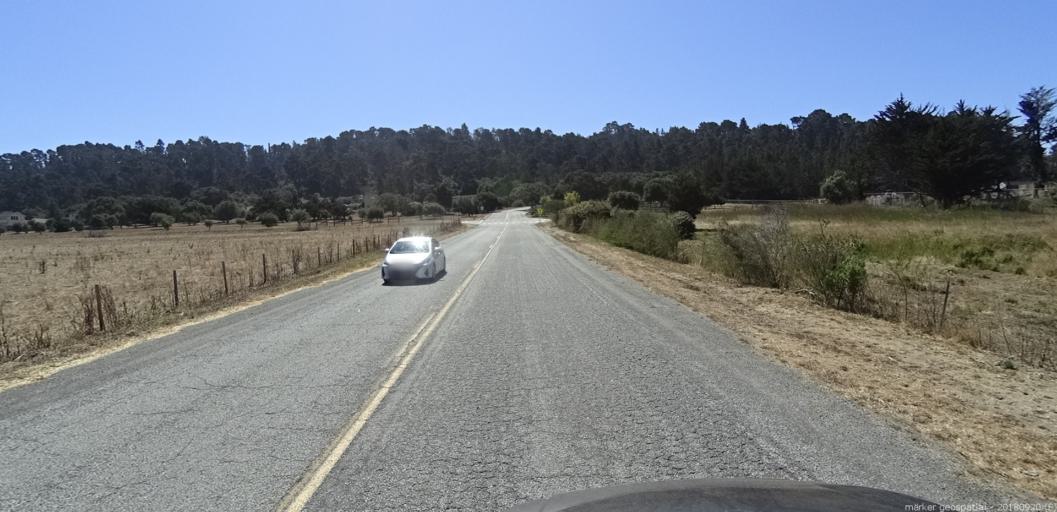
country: US
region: California
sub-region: Monterey County
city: Del Rey Oaks
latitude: 36.5802
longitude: -121.8499
